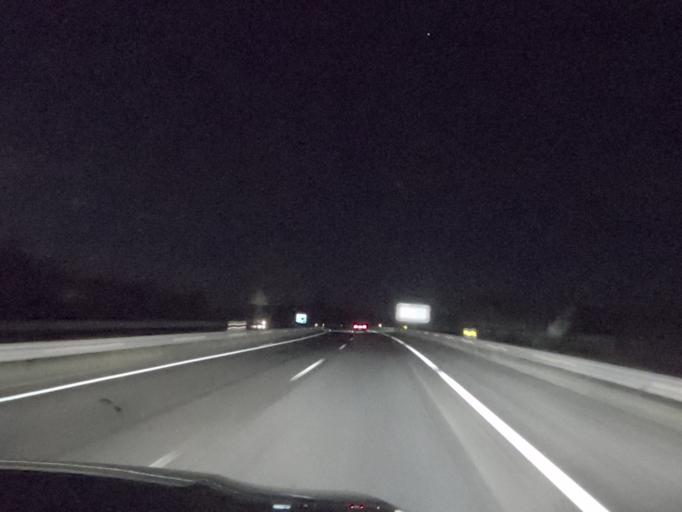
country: ES
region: Galicia
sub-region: Provincia de Ourense
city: Taboadela
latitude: 42.2109
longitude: -7.8344
